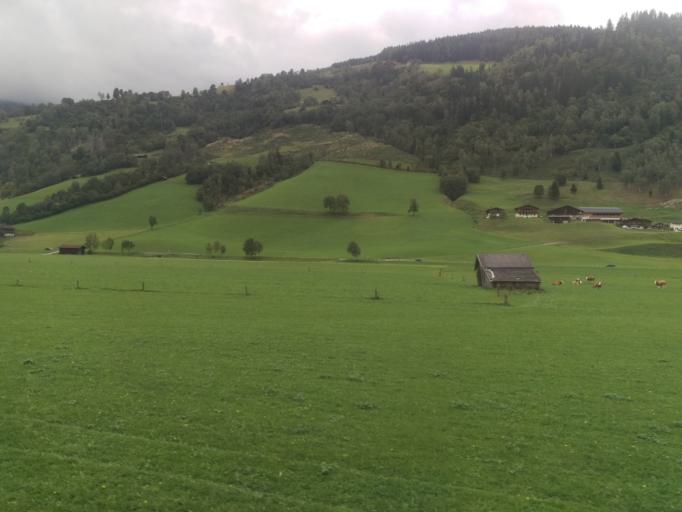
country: AT
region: Salzburg
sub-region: Politischer Bezirk Zell am See
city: Niedernsill
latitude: 47.2821
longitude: 12.6649
